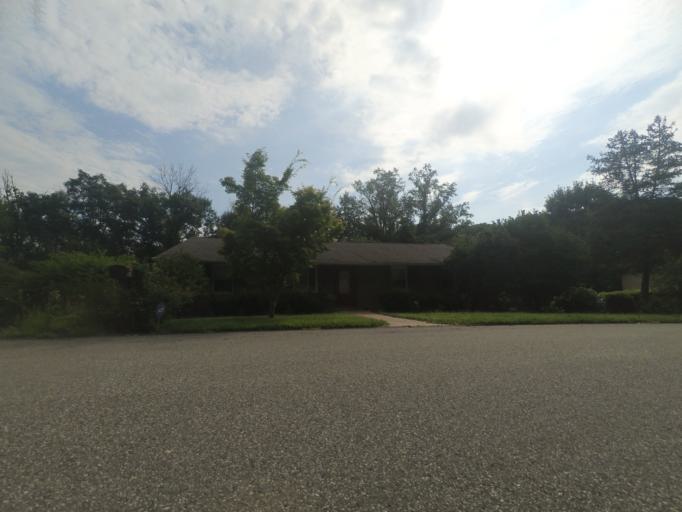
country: US
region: West Virginia
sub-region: Cabell County
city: Huntington
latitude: 38.4010
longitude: -82.4173
